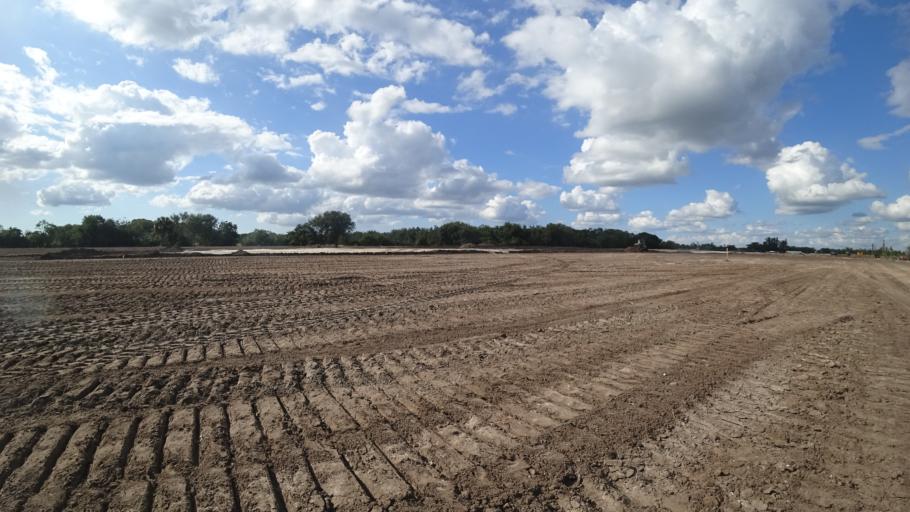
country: US
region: Florida
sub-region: Sarasota County
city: The Meadows
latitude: 27.4655
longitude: -82.3903
